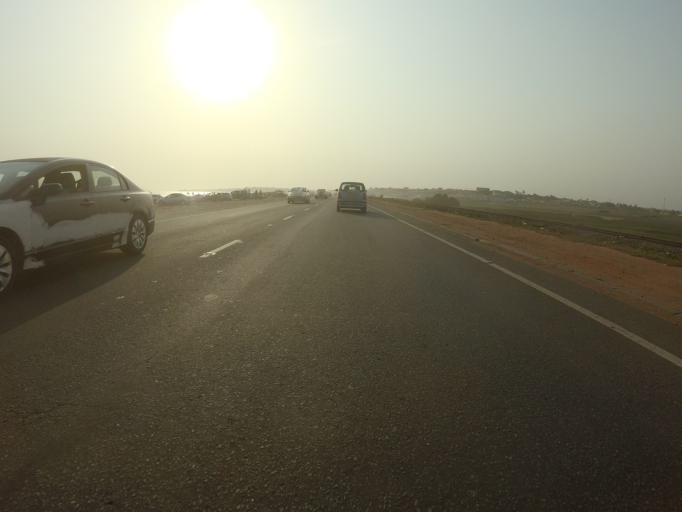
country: GH
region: Greater Accra
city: Nungua
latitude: 5.6127
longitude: -0.0396
